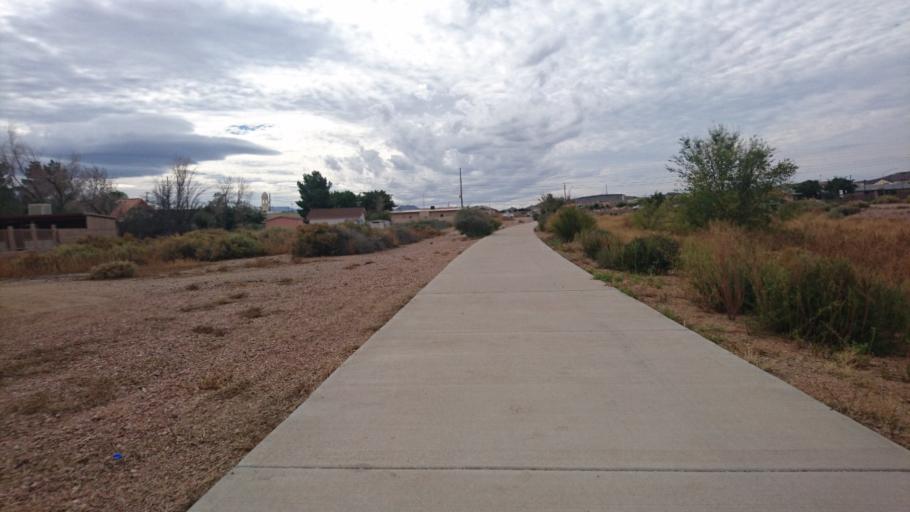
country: US
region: Arizona
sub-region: Mohave County
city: New Kingman-Butler
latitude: 35.2268
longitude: -114.0300
